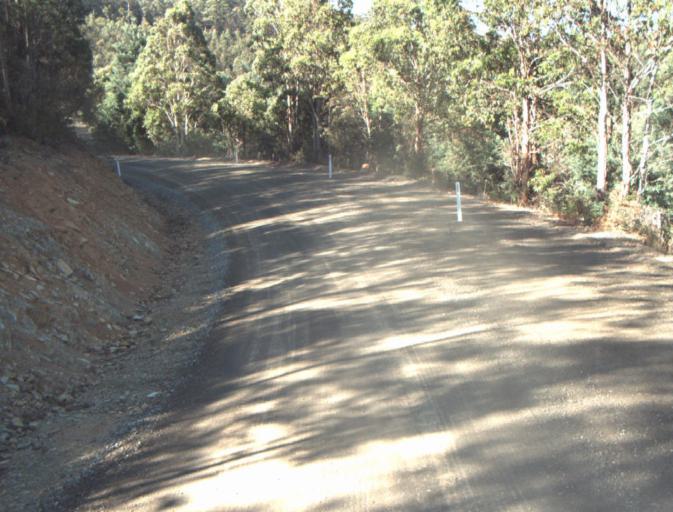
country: AU
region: Tasmania
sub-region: Dorset
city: Scottsdale
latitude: -41.2926
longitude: 147.3407
